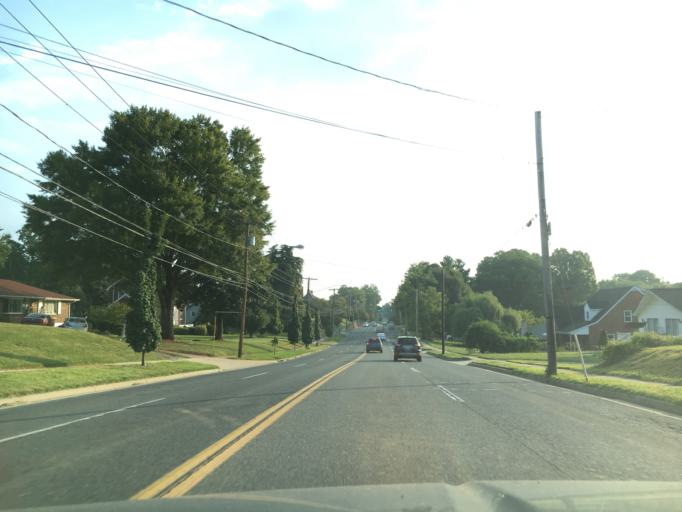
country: US
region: Virginia
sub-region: City of Lynchburg
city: West Lynchburg
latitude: 37.3827
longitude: -79.1803
